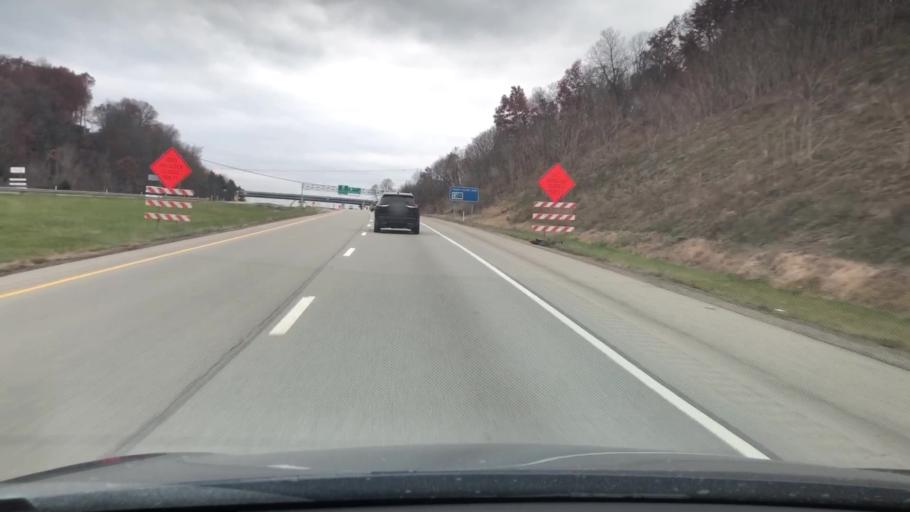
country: US
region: Pennsylvania
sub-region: Armstrong County
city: West Kittanning
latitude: 40.8075
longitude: -79.5420
